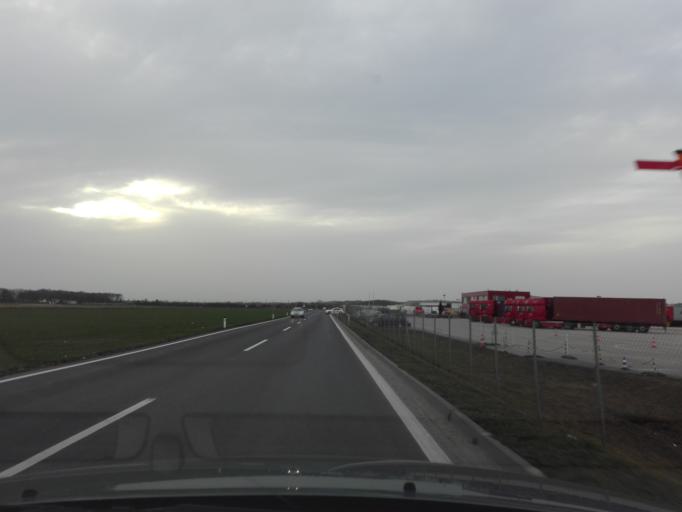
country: AT
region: Upper Austria
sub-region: Politischer Bezirk Linz-Land
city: Horsching
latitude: 48.2351
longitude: 14.1737
